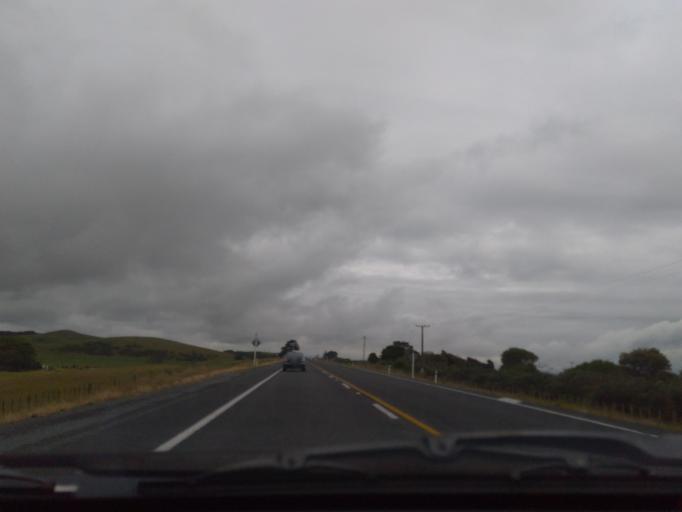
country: NZ
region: Northland
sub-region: Whangarei
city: Ruakaka
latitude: -35.9290
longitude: 174.4544
